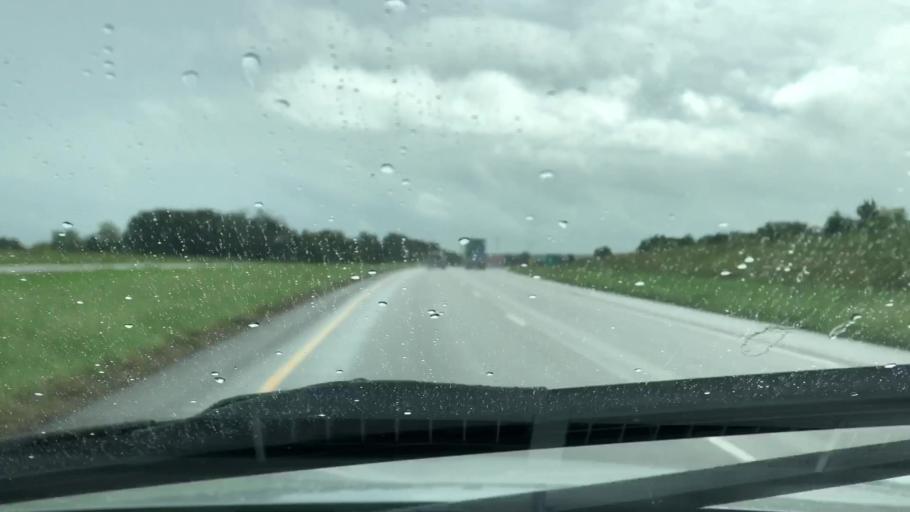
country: US
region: Texas
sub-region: Fayette County
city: Schulenburg
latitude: 29.6964
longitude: -96.8557
